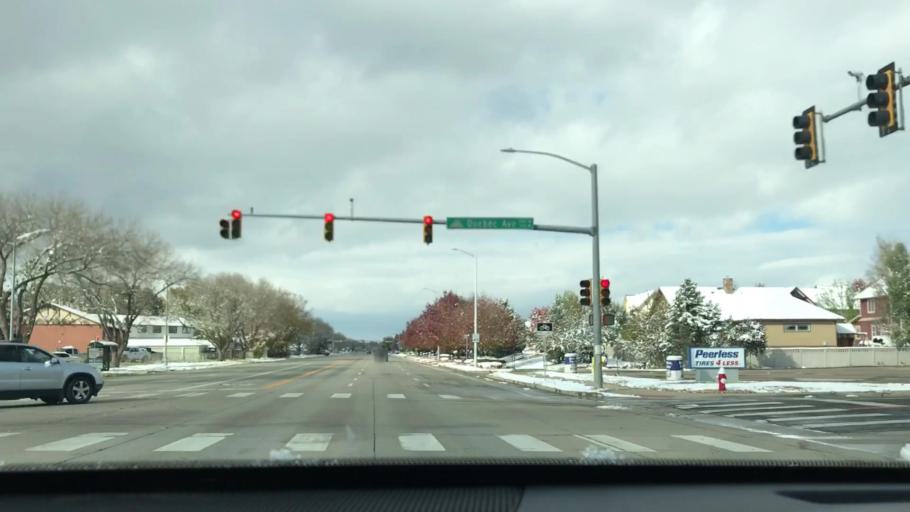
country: US
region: Colorado
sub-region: Boulder County
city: Longmont
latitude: 40.1409
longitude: -105.1024
